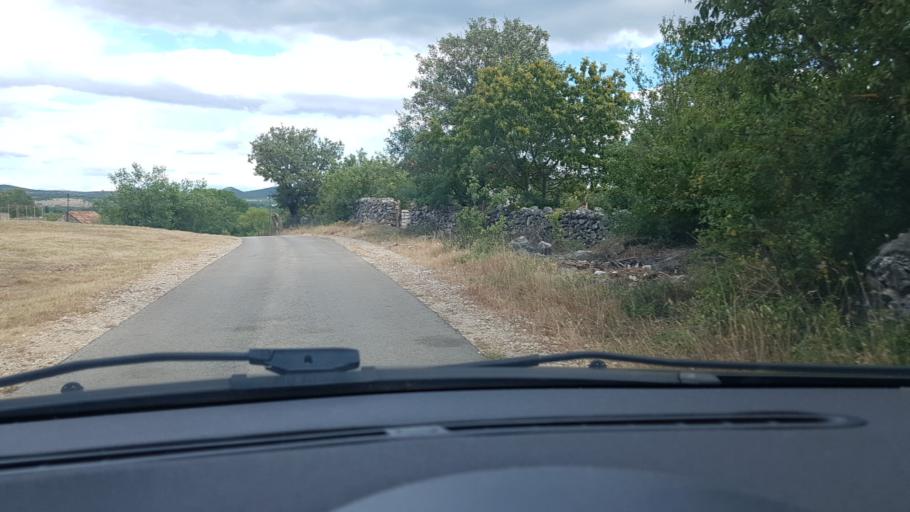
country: HR
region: Sibensko-Kniniska
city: Kistanje
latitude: 44.1103
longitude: 15.9252
